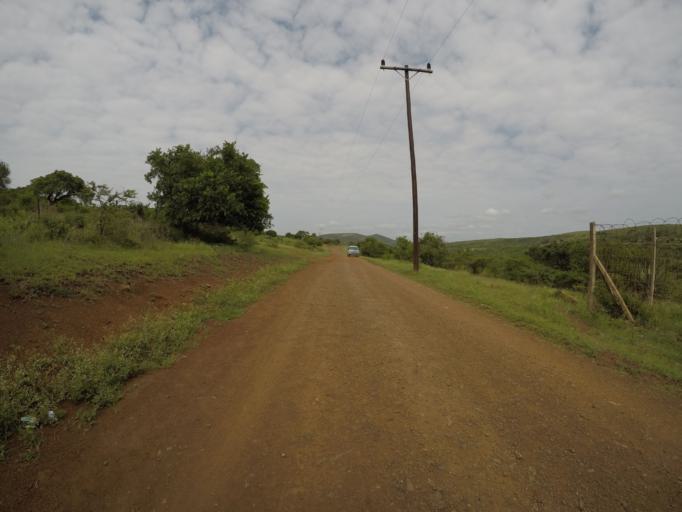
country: ZA
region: KwaZulu-Natal
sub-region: uThungulu District Municipality
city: Empangeni
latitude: -28.6217
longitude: 31.9036
